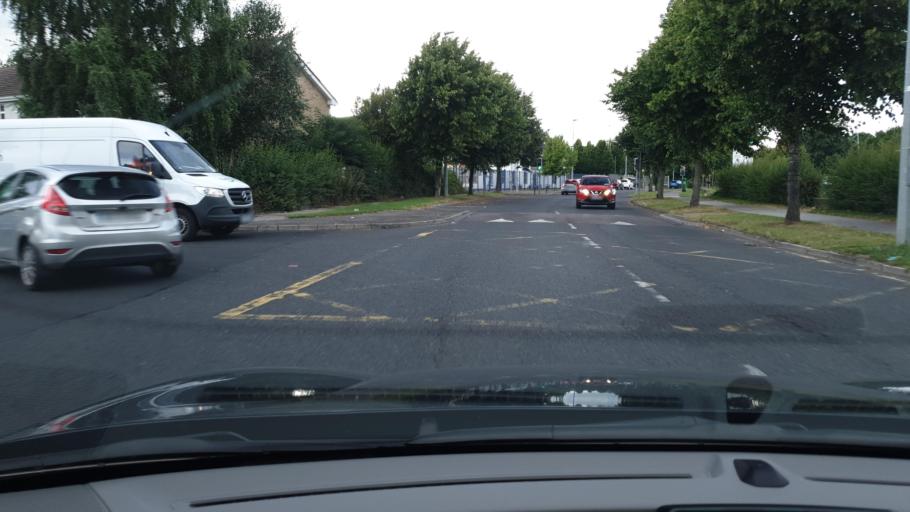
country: IE
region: Leinster
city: Clondalkin
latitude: 53.3238
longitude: -6.4114
